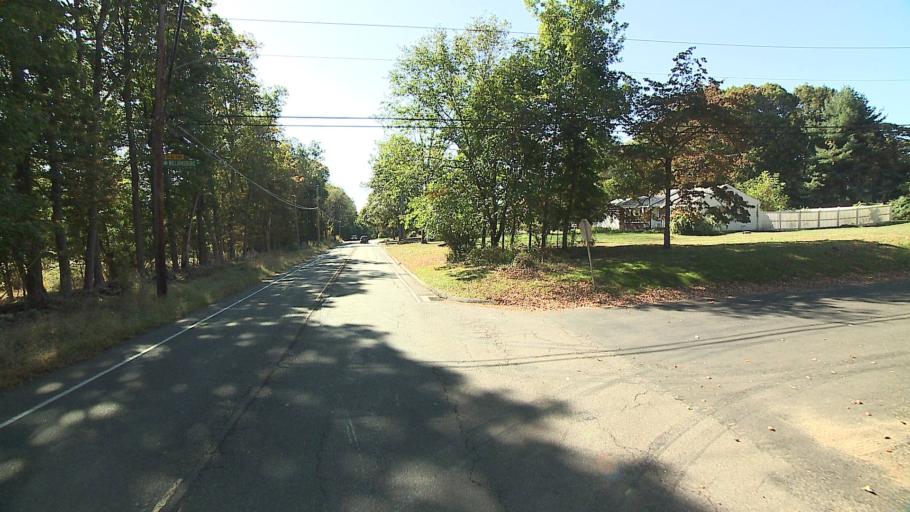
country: US
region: Connecticut
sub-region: New Haven County
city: Orange
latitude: 41.3104
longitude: -73.0204
